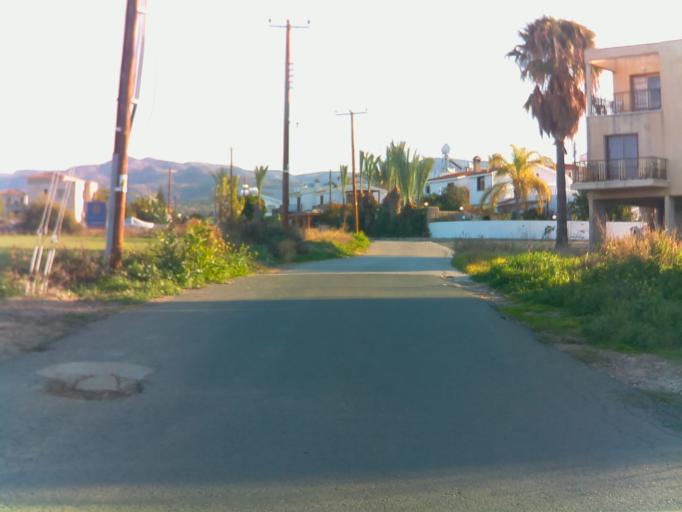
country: CY
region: Pafos
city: Pegeia
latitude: 34.8578
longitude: 32.3775
